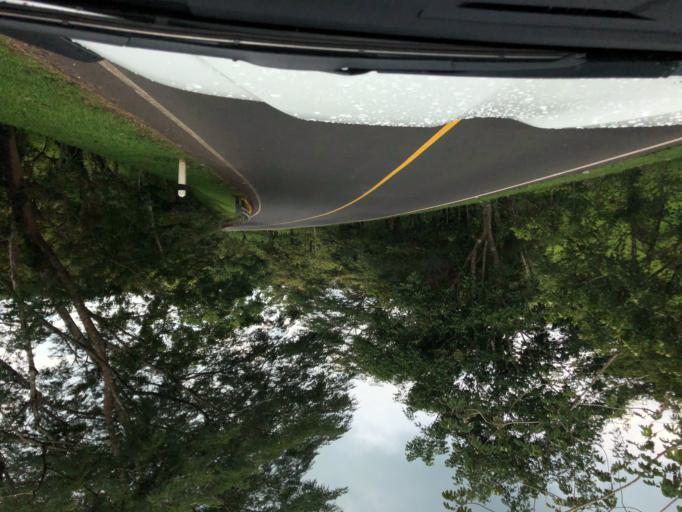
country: NI
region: Chontales
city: Villa Sandino
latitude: 11.9970
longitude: -84.8912
